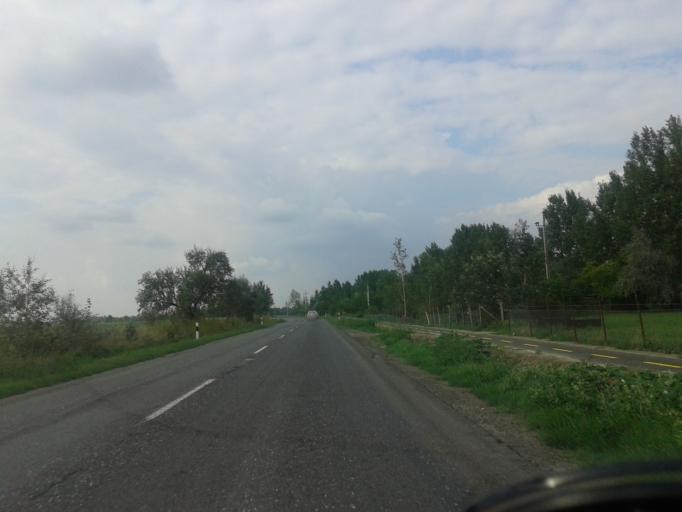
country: HU
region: Bacs-Kiskun
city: Akaszto
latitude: 46.7084
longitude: 19.1872
